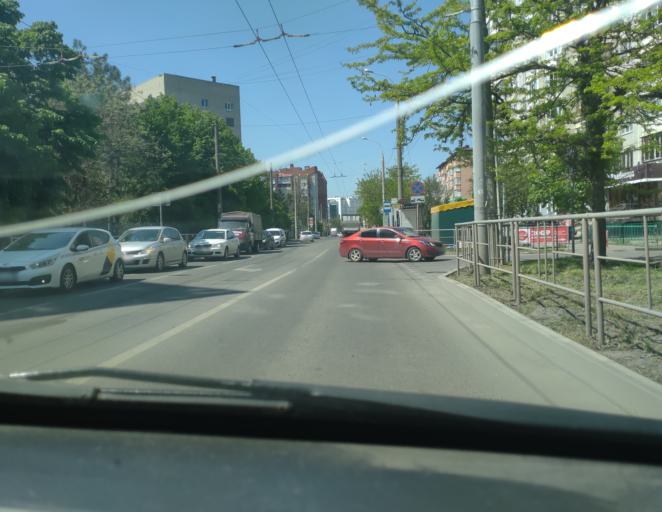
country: RU
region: Krasnodarskiy
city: Krasnodar
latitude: 45.0657
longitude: 39.0244
